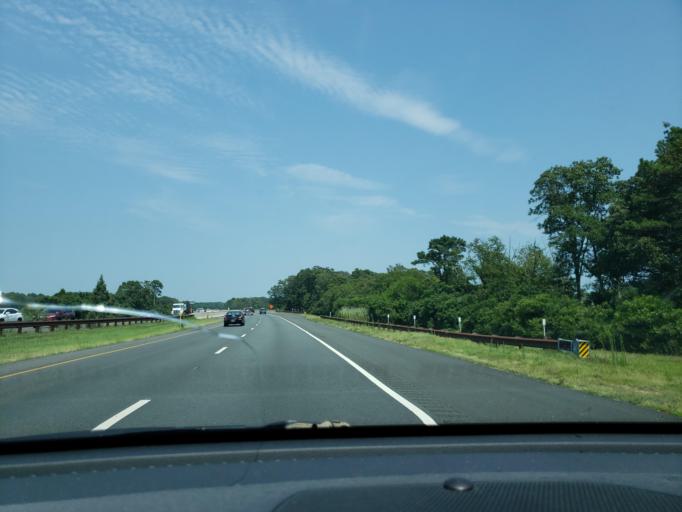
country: US
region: New Jersey
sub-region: Atlantic County
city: Somers Point
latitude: 39.3314
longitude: -74.6091
